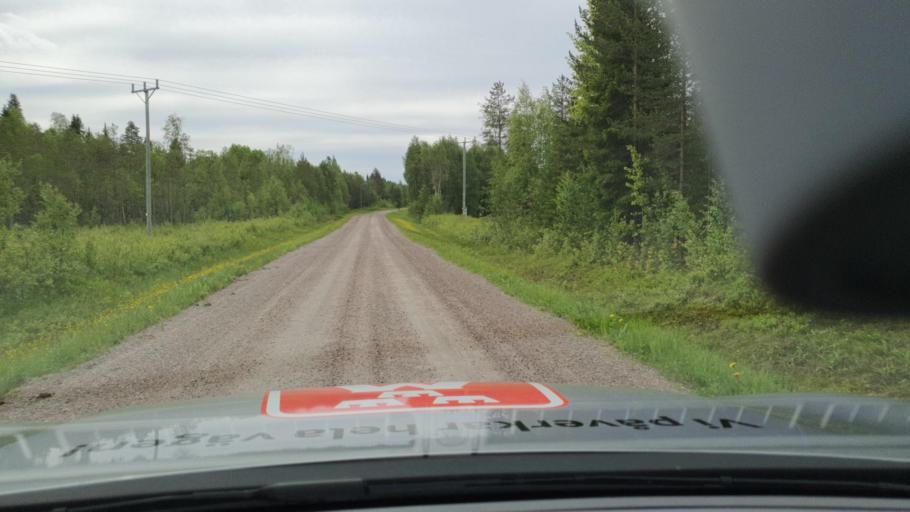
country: SE
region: Norrbotten
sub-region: Kalix Kommun
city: Kalix
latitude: 66.0104
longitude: 23.4518
